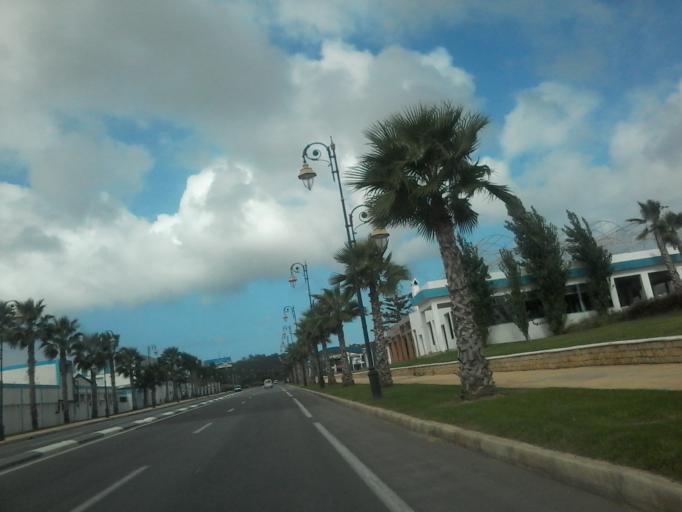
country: MA
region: Tanger-Tetouan
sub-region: Tetouan
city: Martil
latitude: 35.6562
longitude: -5.3191
